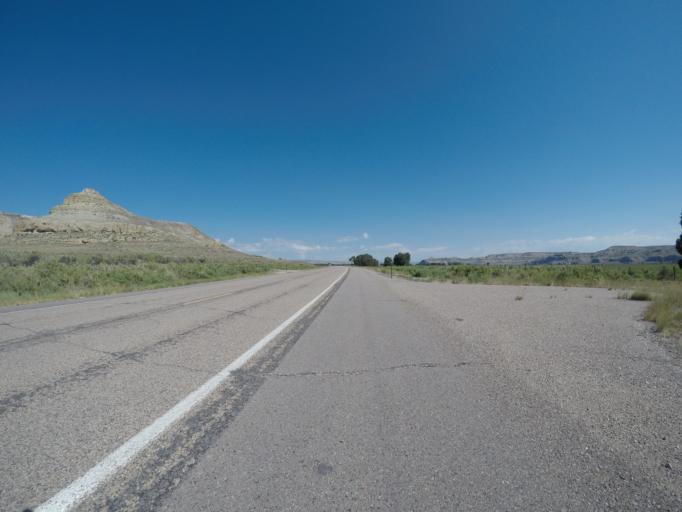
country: US
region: Wyoming
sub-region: Sublette County
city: Marbleton
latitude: 42.1999
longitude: -110.1790
